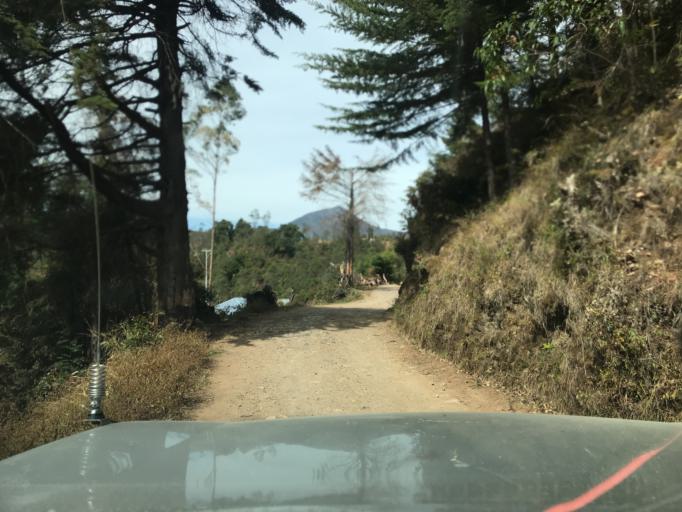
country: TL
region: Ainaro
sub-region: Ainaro
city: Ainaro
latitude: -8.8818
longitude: 125.5407
